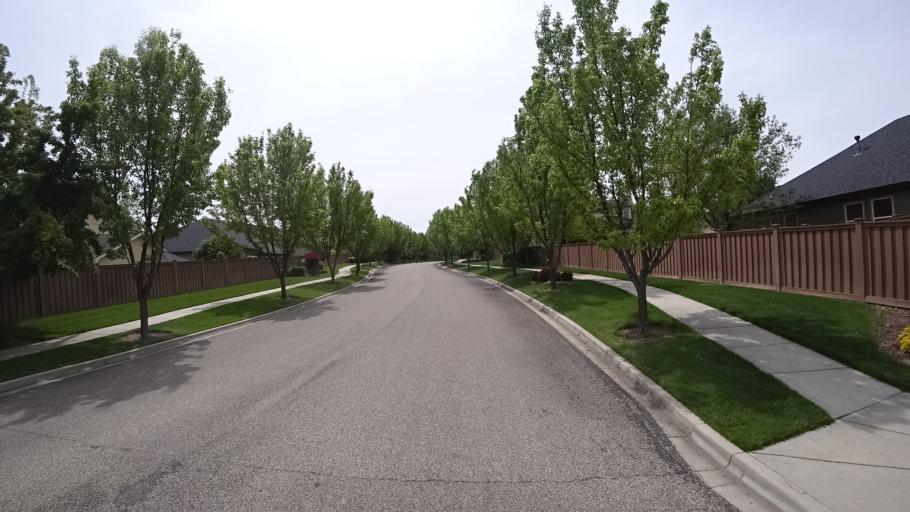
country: US
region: Idaho
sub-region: Ada County
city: Meridian
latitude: 43.5598
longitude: -116.3246
